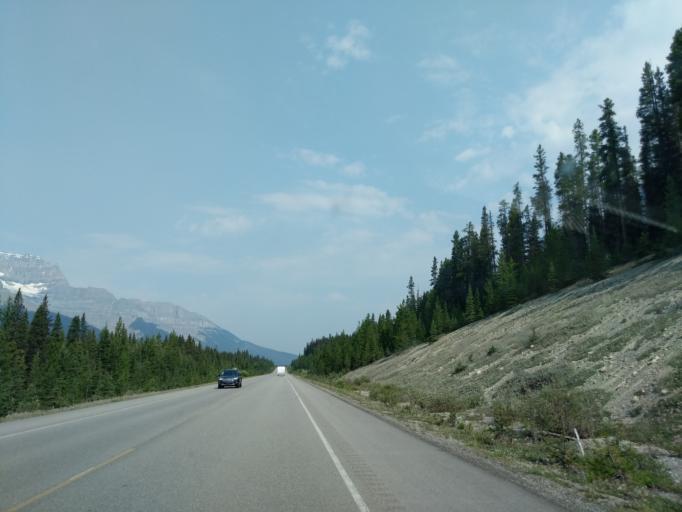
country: CA
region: Alberta
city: Lake Louise
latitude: 51.8652
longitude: -116.6643
